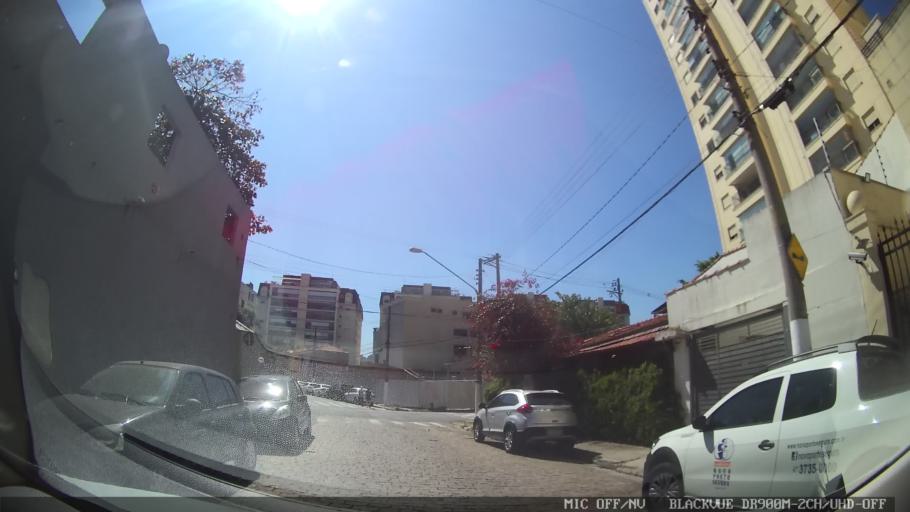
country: BR
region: Sao Paulo
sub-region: Sao Paulo
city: Sao Paulo
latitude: -23.5099
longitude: -46.6523
